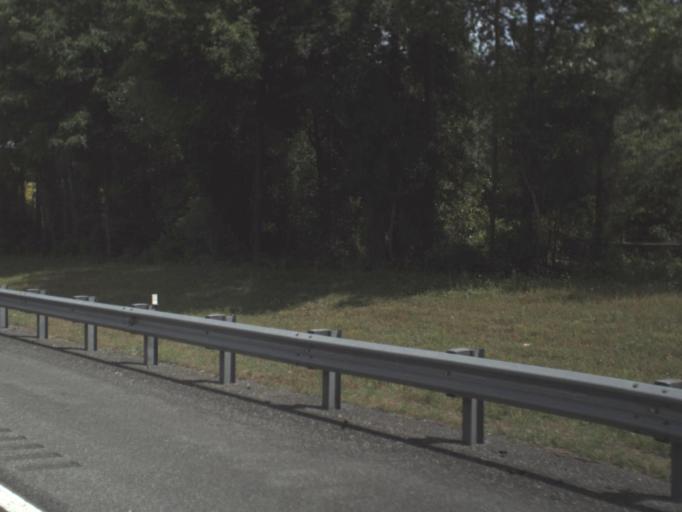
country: US
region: Florida
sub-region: Suwannee County
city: Live Oak
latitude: 30.3434
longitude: -83.1326
